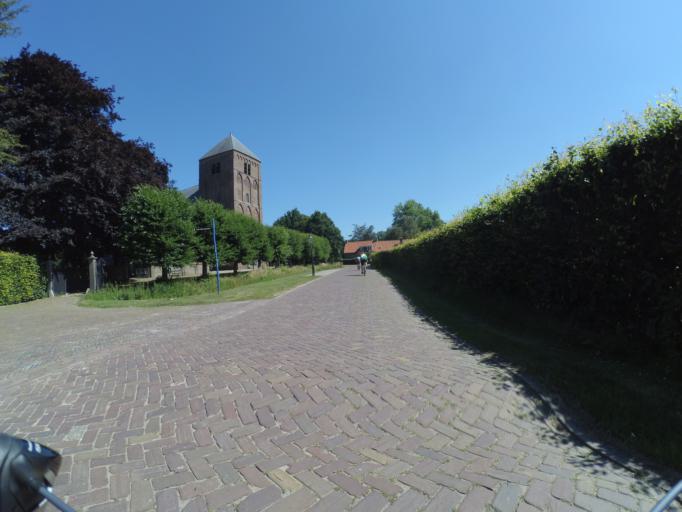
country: NL
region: North Brabant
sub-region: Gemeente Waalwijk
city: Waspik
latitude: 51.6942
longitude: 4.9040
